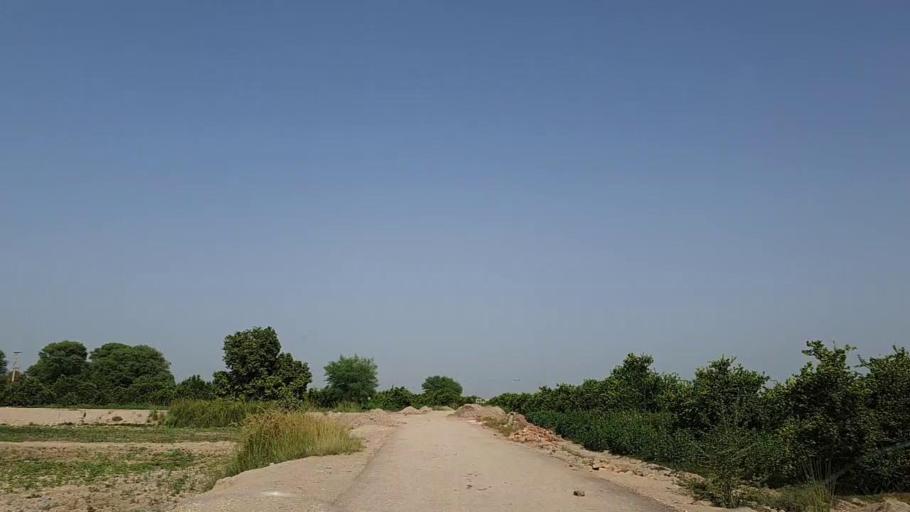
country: PK
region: Sindh
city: Kandiaro
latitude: 27.0729
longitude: 68.1369
